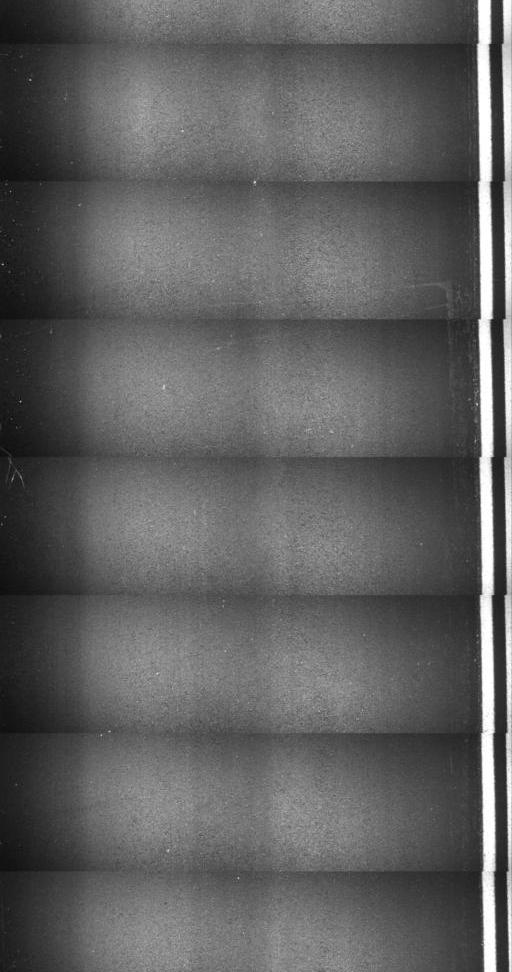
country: US
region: Vermont
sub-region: Windsor County
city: Woodstock
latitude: 43.5789
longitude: -72.5153
